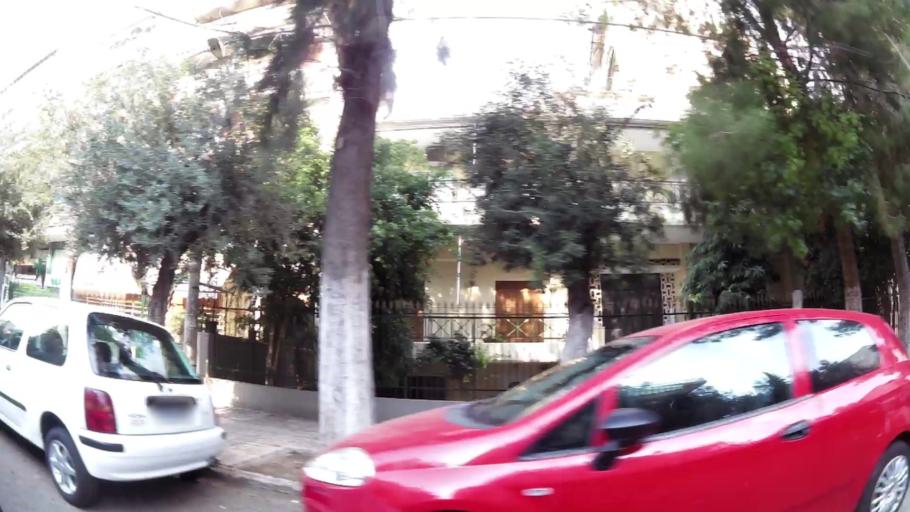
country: GR
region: Attica
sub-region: Nomarchia Athinas
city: Kallithea
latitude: 37.9473
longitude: 23.6945
